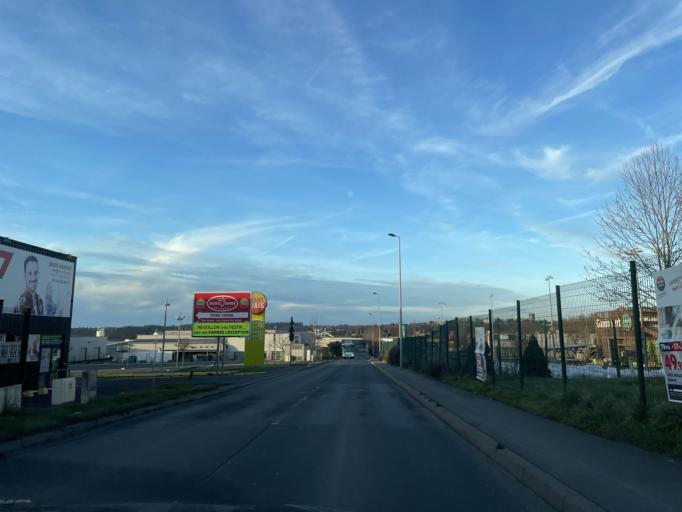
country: FR
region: Ile-de-France
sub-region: Departement de Seine-et-Marne
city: Coulommiers
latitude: 48.8024
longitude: 3.0973
